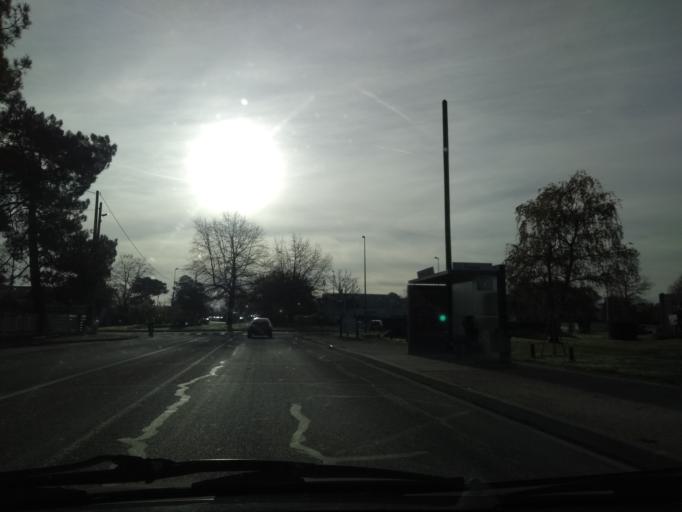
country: FR
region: Aquitaine
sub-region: Departement de la Gironde
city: Canejan
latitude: 44.7840
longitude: -0.6530
